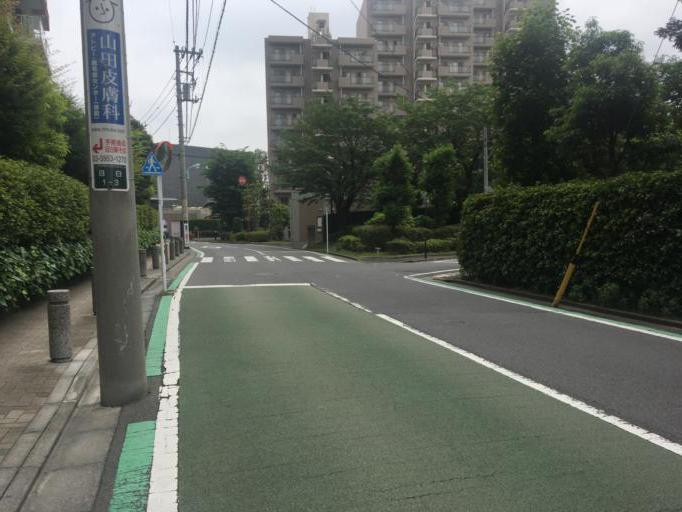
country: JP
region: Tokyo
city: Tokyo
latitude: 35.7172
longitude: 139.7066
